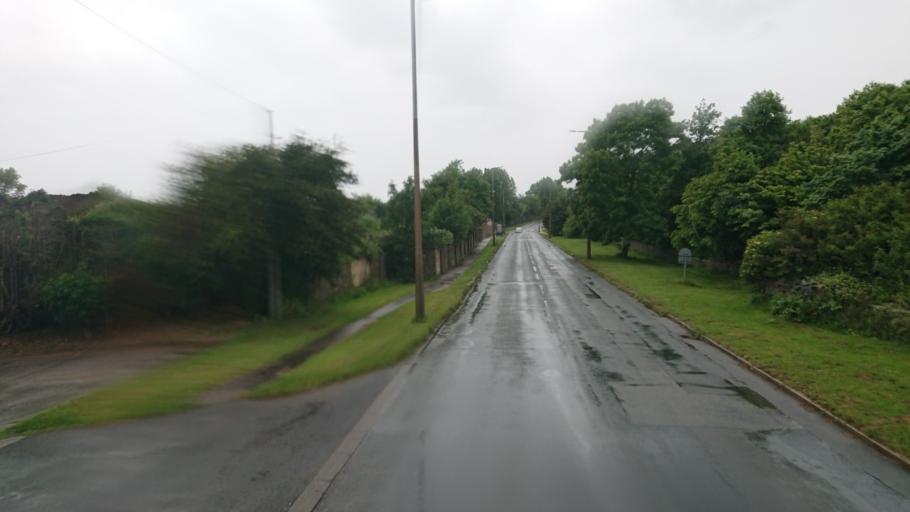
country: GB
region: England
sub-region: Lancashire
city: Morecambe
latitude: 54.0289
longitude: -2.8915
